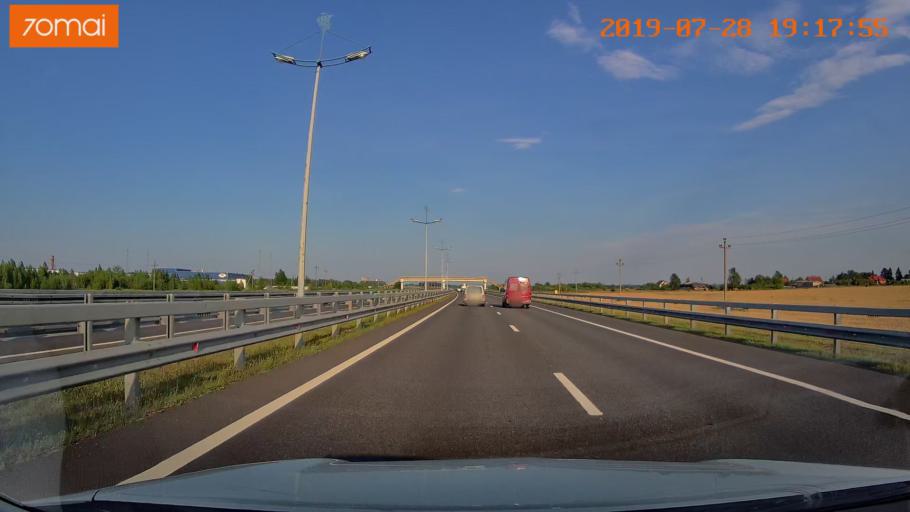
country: RU
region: Kaliningrad
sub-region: Zelenogradskiy Rayon
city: Zelenogradsk
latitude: 54.9198
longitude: 20.4159
